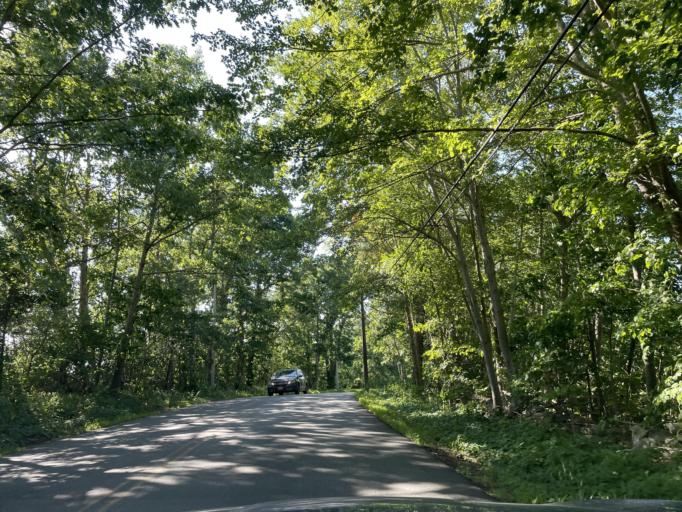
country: US
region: Massachusetts
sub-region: Worcester County
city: East Brookfield
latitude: 42.1668
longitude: -72.0277
